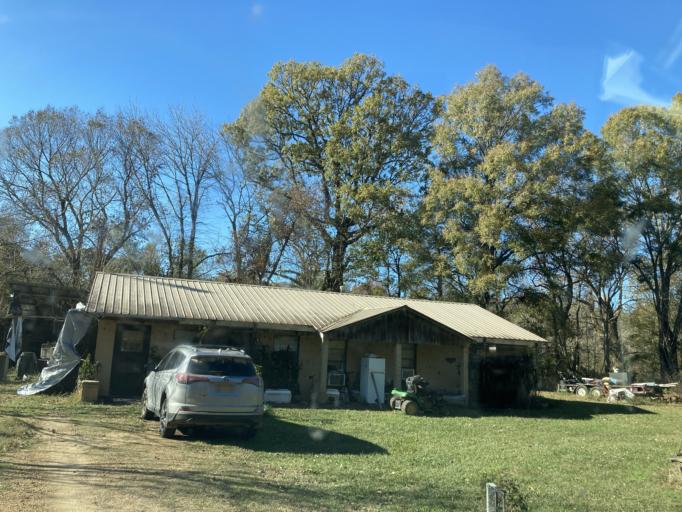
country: US
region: Mississippi
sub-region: Sharkey County
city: Rolling Fork
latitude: 32.7593
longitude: -90.6884
